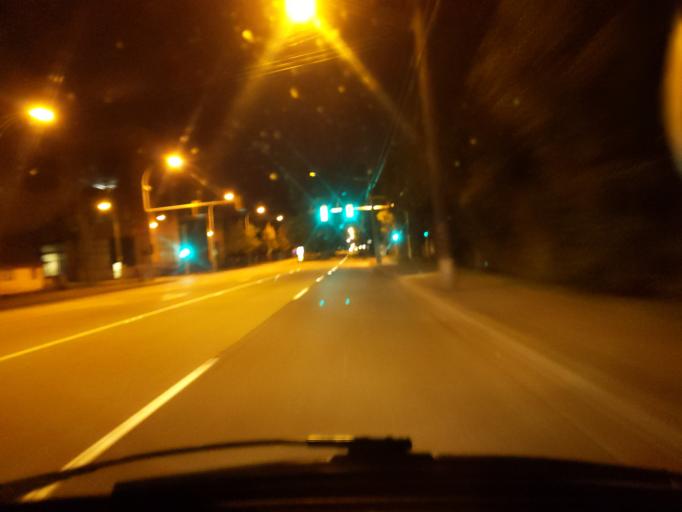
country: CA
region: British Columbia
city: New Westminster
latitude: 49.1916
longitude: -122.8278
